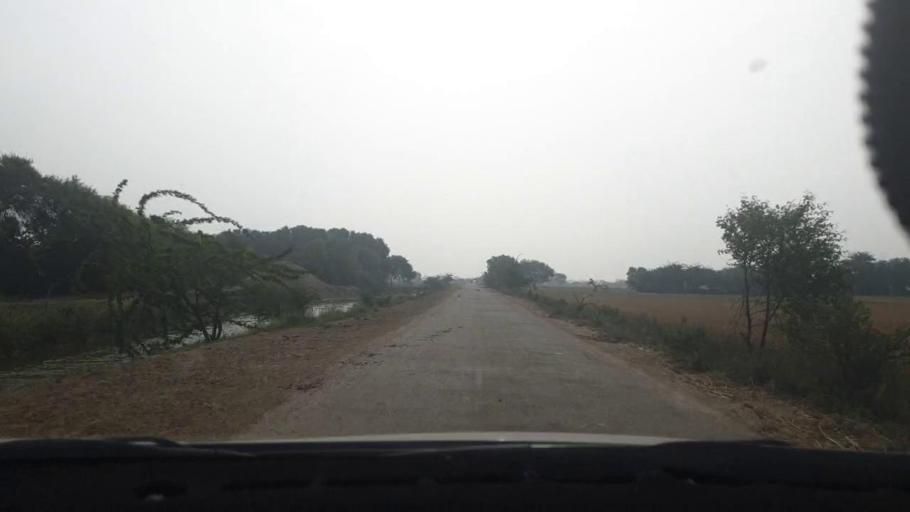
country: PK
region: Sindh
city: Tando Muhammad Khan
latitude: 25.0593
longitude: 68.5449
